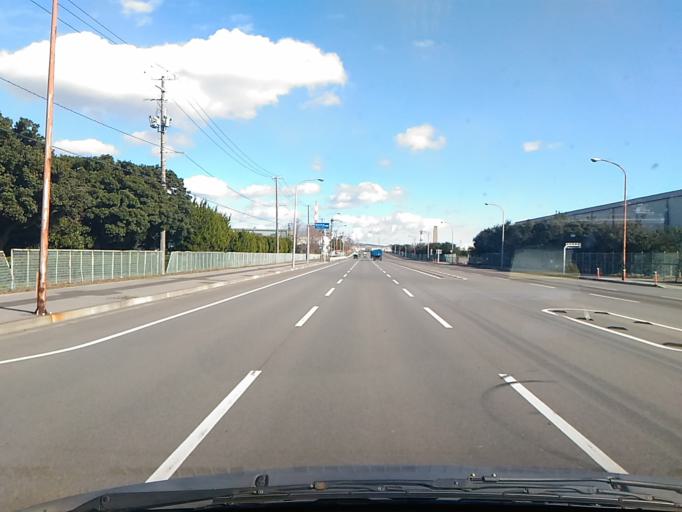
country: JP
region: Fukushima
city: Iwaki
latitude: 36.9320
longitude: 140.8657
